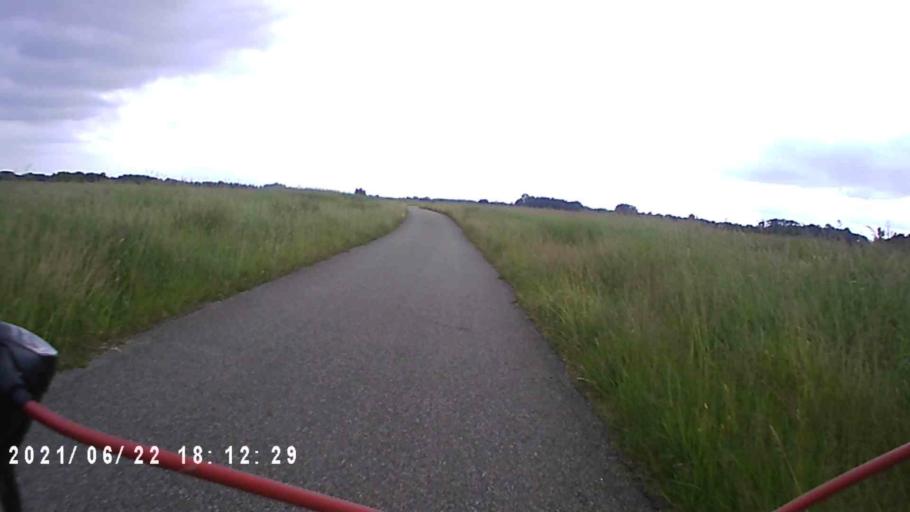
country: NL
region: Groningen
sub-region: Gemeente Zuidhorn
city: Aduard
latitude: 53.1760
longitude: 6.4902
